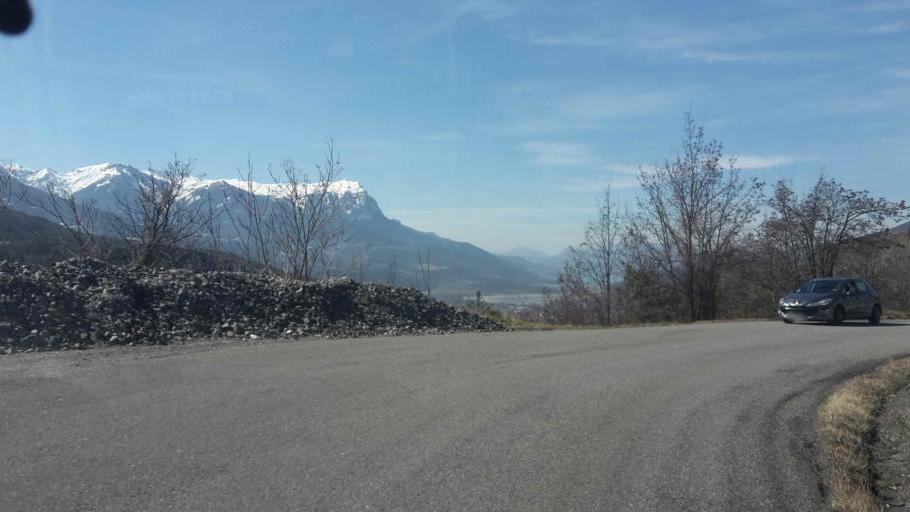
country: FR
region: Provence-Alpes-Cote d'Azur
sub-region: Departement des Hautes-Alpes
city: Embrun
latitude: 44.5662
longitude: 6.5411
